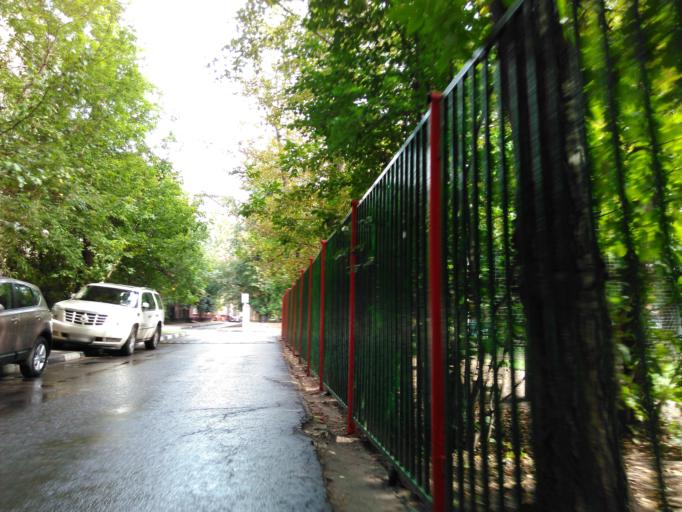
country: RU
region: Moskovskaya
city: Semenovskoye
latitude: 55.6848
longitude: 37.5650
